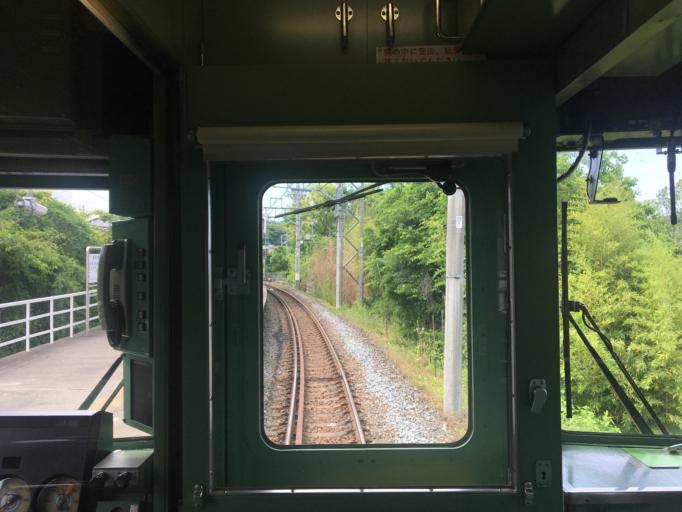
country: JP
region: Saitama
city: Yorii
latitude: 36.1169
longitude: 139.2005
